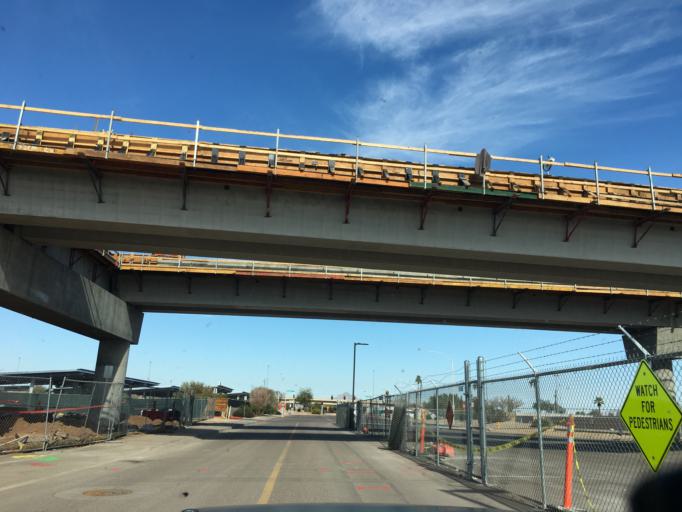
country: US
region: Arizona
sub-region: Maricopa County
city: Phoenix
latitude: 33.4350
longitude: -112.0304
